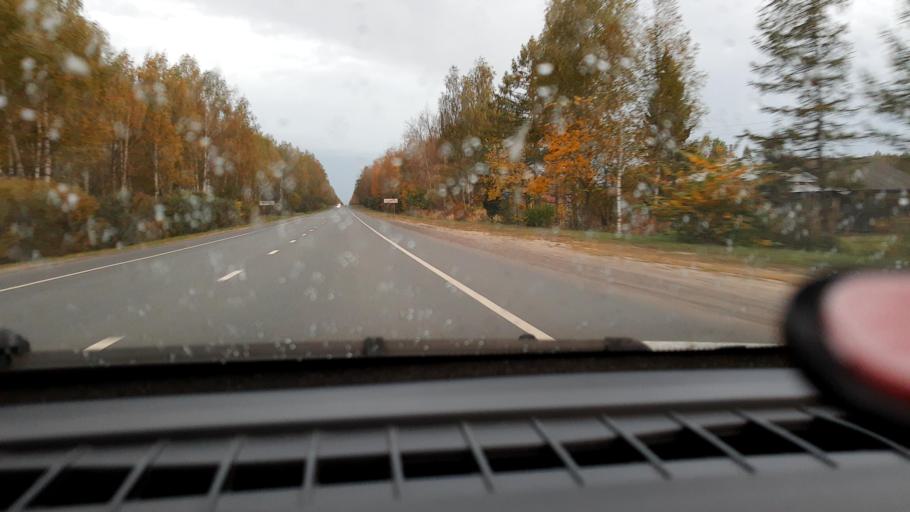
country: RU
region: Vladimir
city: Orgtrud
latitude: 56.2036
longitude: 40.7495
